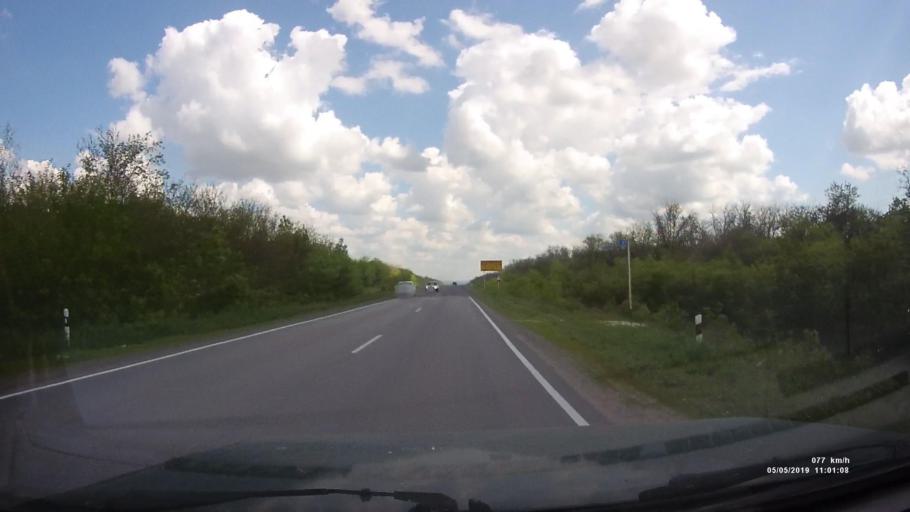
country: RU
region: Rostov
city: Ust'-Donetskiy
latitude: 47.6776
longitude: 40.8958
